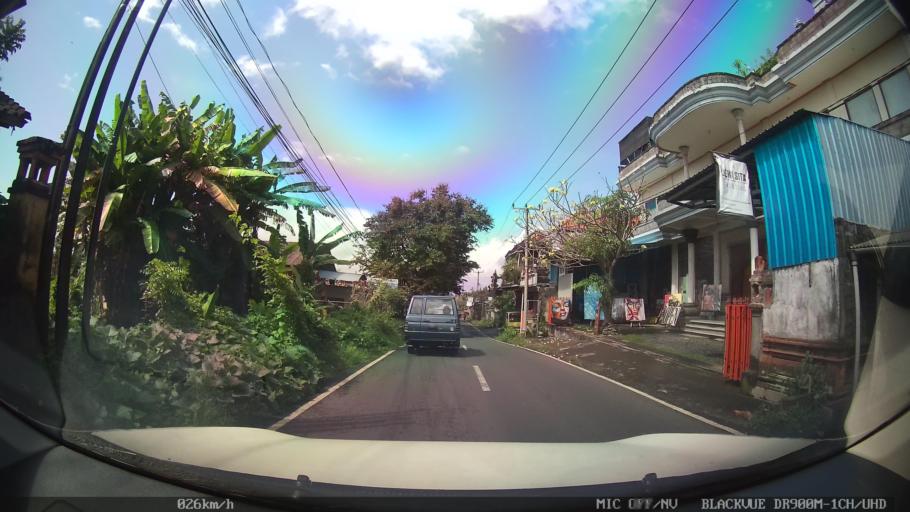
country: ID
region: Bali
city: Banjar Tebongkang
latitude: -8.5464
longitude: 115.2621
